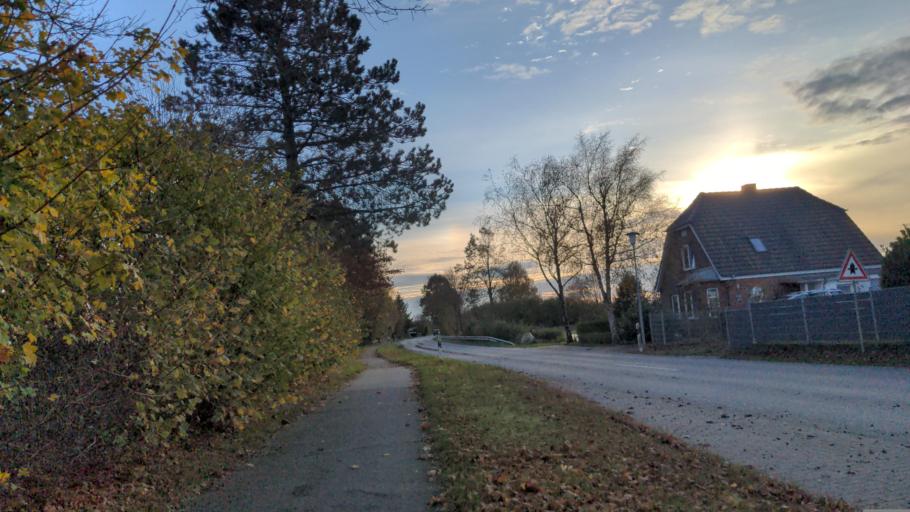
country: DE
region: Schleswig-Holstein
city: Rehhorst
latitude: 53.8675
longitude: 10.4703
